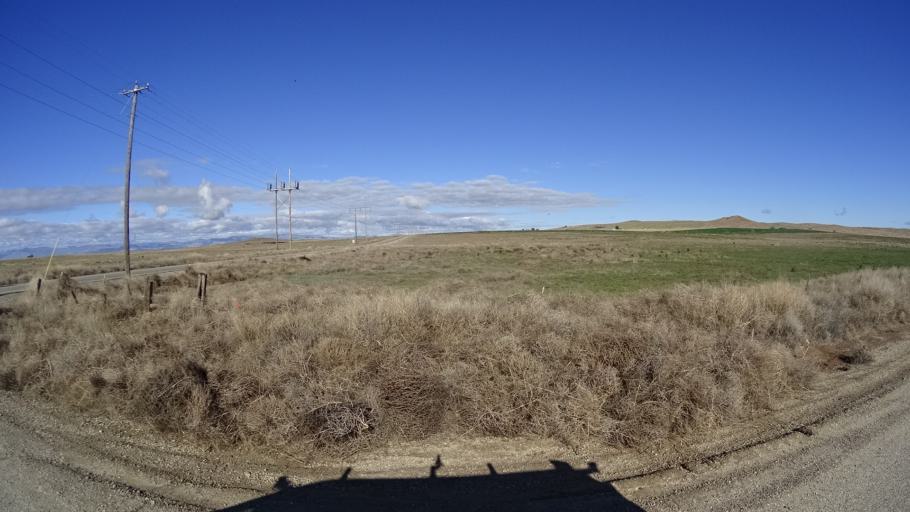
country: US
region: Idaho
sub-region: Ada County
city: Kuna
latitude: 43.4229
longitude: -116.4140
